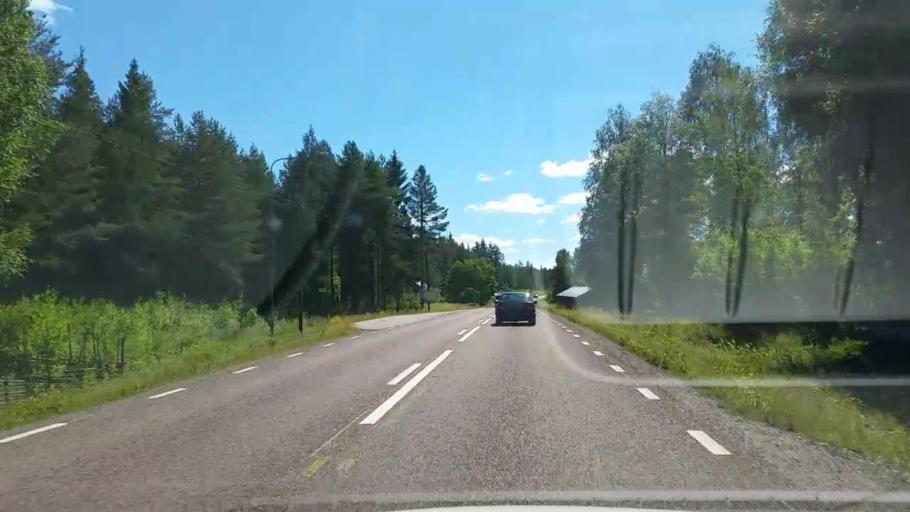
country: SE
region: Gaevleborg
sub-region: Ovanakers Kommun
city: Edsbyn
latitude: 61.2711
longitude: 15.8932
